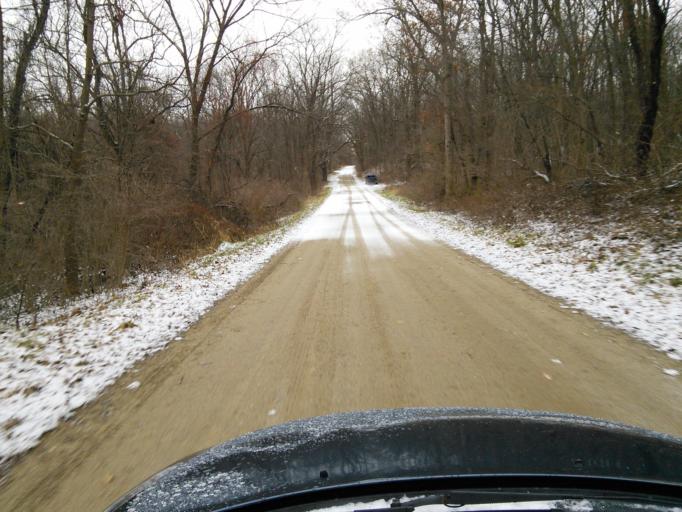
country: US
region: Michigan
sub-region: Jackson County
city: Grass Lake
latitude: 42.3106
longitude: -84.1929
